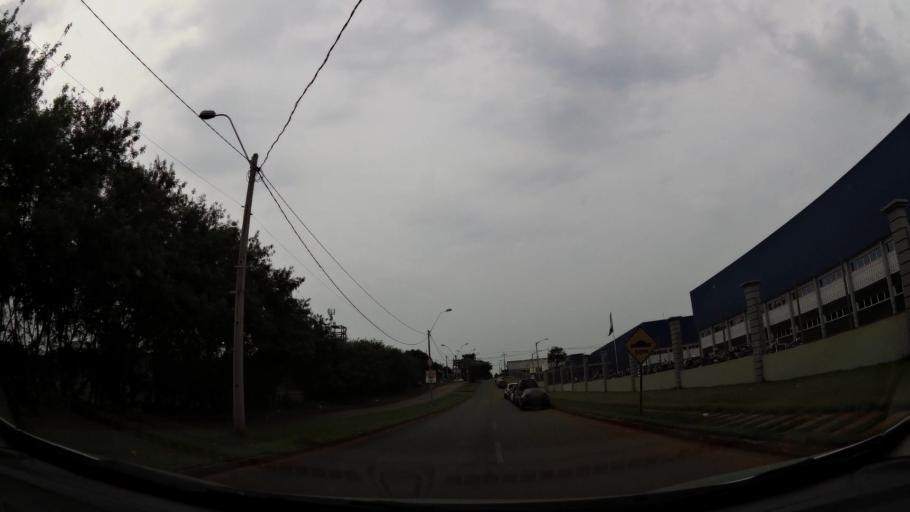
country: PY
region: Alto Parana
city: Presidente Franco
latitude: -25.5316
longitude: -54.6484
